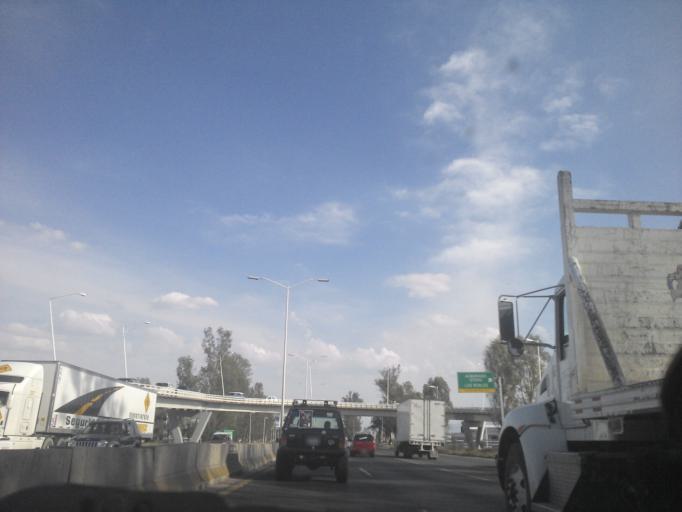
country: MX
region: Jalisco
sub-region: Tlajomulco de Zuniga
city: Palomar
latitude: 20.6387
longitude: -103.4393
